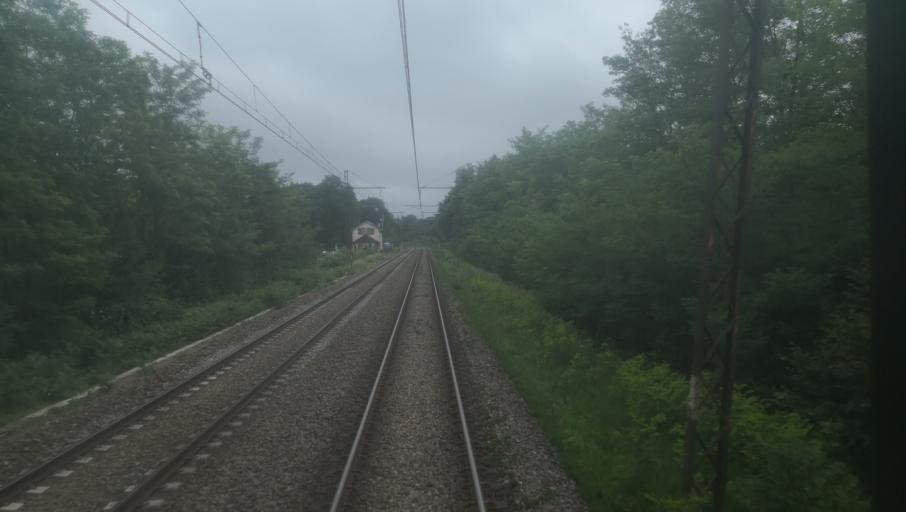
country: FR
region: Limousin
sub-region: Departement de la Creuse
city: Saint-Maurice-la-Souterraine
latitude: 46.1791
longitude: 1.4466
